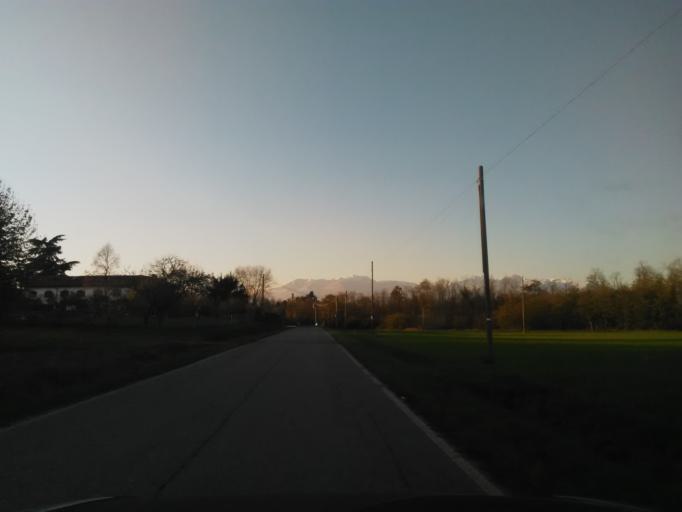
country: IT
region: Piedmont
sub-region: Provincia di Biella
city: Cerrione
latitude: 45.4630
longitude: 8.0762
